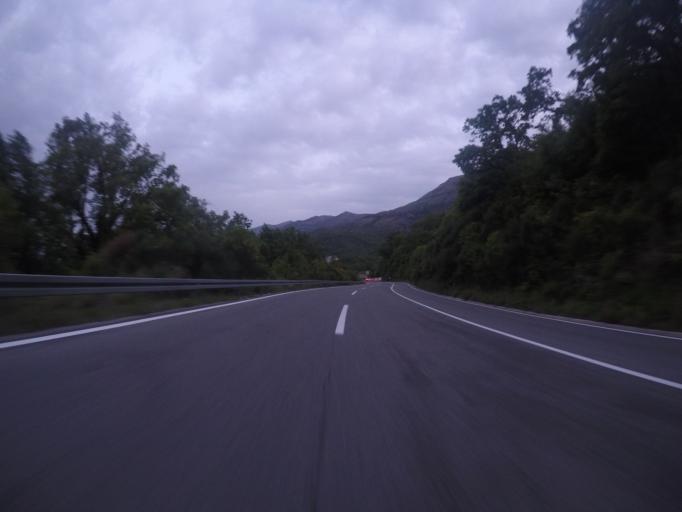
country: ME
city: Petrovac na Moru
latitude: 42.1930
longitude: 18.9844
